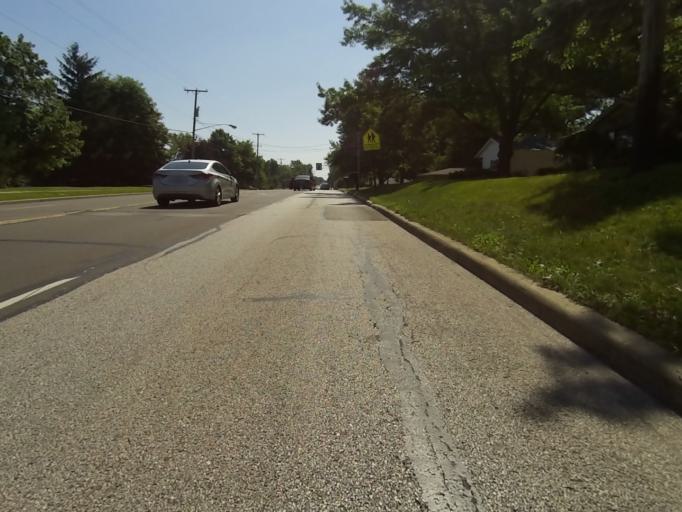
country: US
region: Ohio
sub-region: Summit County
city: Silver Lake
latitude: 41.1667
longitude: -81.4512
